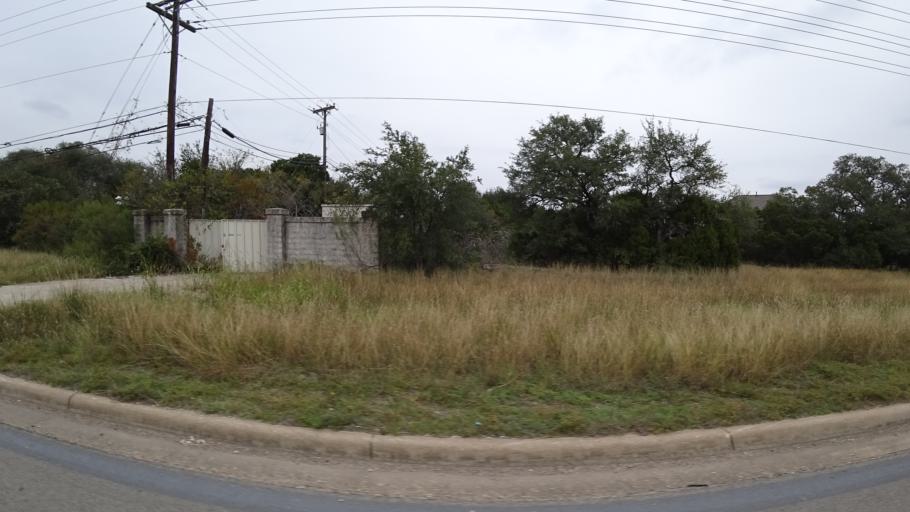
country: US
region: Texas
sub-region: Travis County
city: Shady Hollow
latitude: 30.1827
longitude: -97.9010
